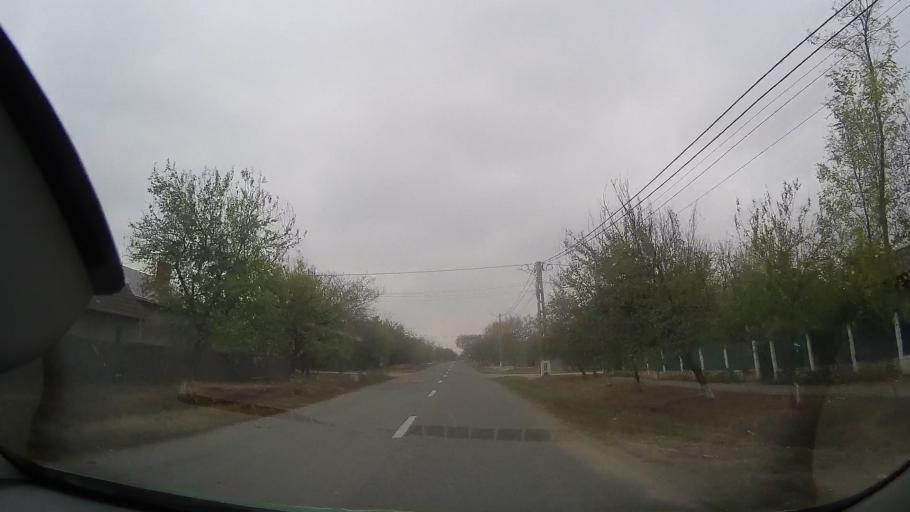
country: RO
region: Ialomita
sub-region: Comuna Valea Macrisului
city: Valea Macrisului
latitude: 44.7466
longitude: 26.8246
